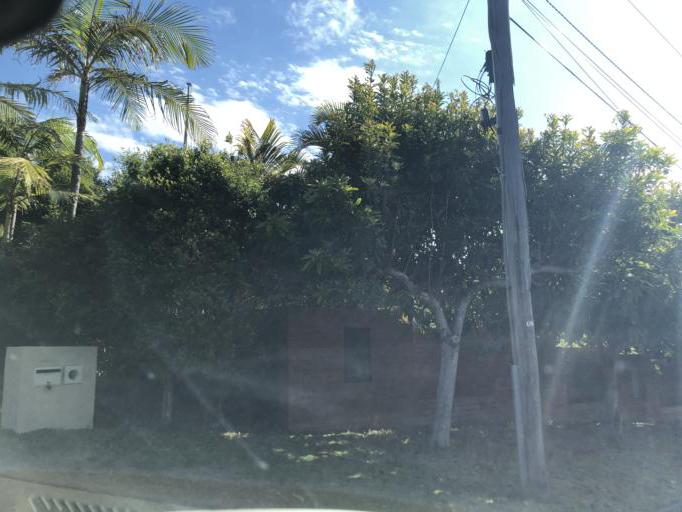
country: AU
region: New South Wales
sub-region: Coffs Harbour
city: Moonee Beach
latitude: -30.2326
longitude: 153.1522
